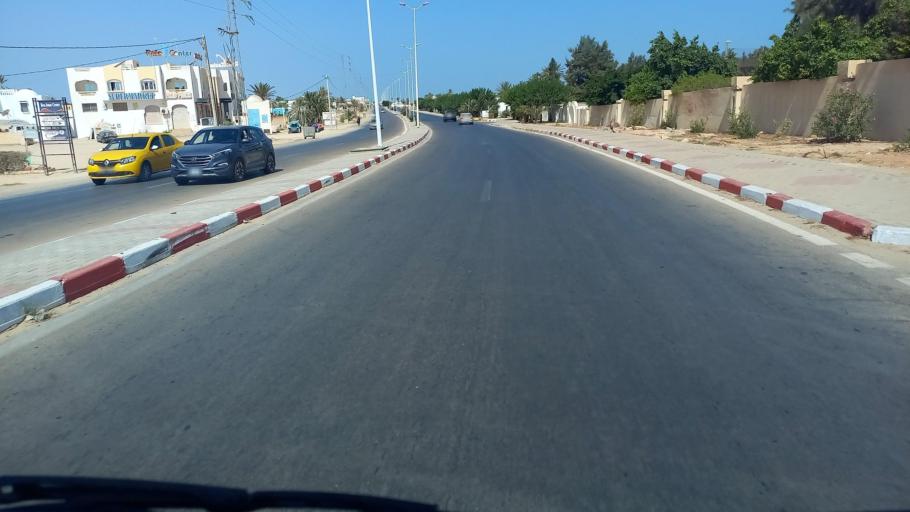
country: TN
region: Madanin
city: Midoun
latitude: 33.8594
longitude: 10.9736
